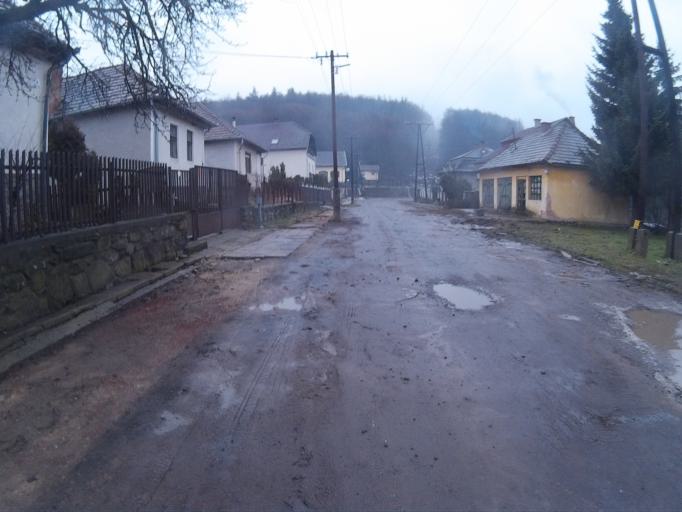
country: HU
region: Nograd
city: Somoskoujfalu
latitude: 48.1674
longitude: 19.8578
